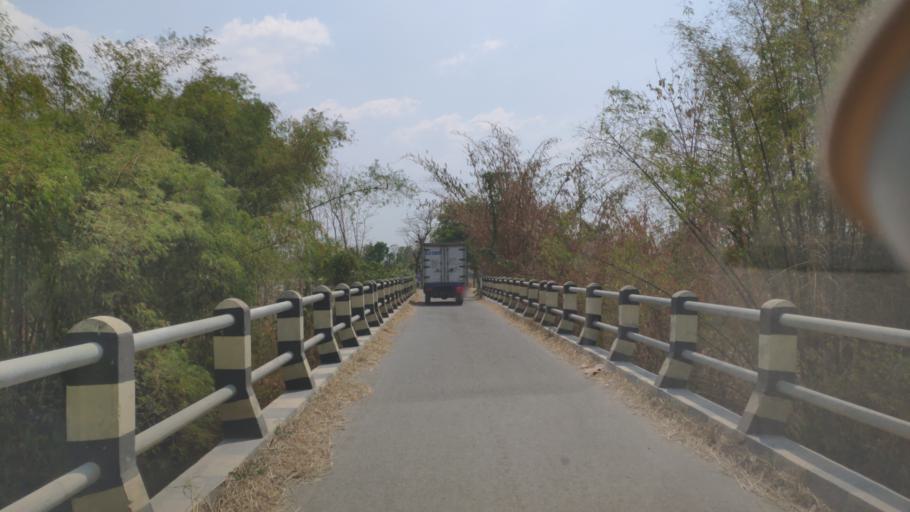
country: ID
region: Central Java
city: Kadengan
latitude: -7.1742
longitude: 111.3896
